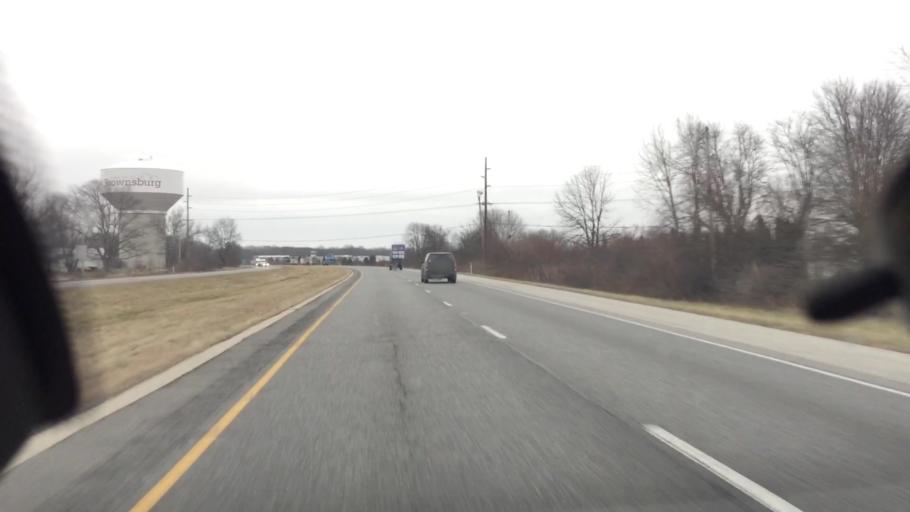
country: US
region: Indiana
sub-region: Hendricks County
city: Brownsburg
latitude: 39.8663
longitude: -86.4157
